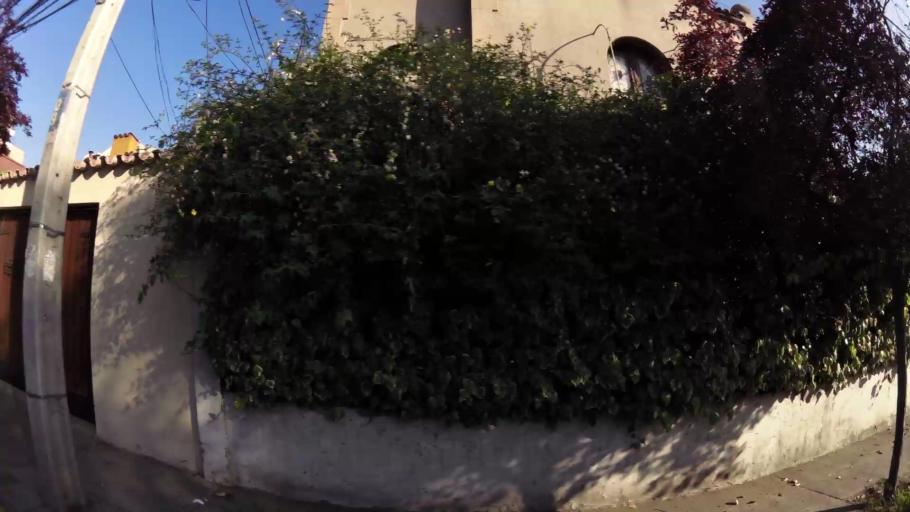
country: CL
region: Santiago Metropolitan
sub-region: Provincia de Santiago
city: Villa Presidente Frei, Nunoa, Santiago, Chile
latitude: -33.4512
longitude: -70.6108
